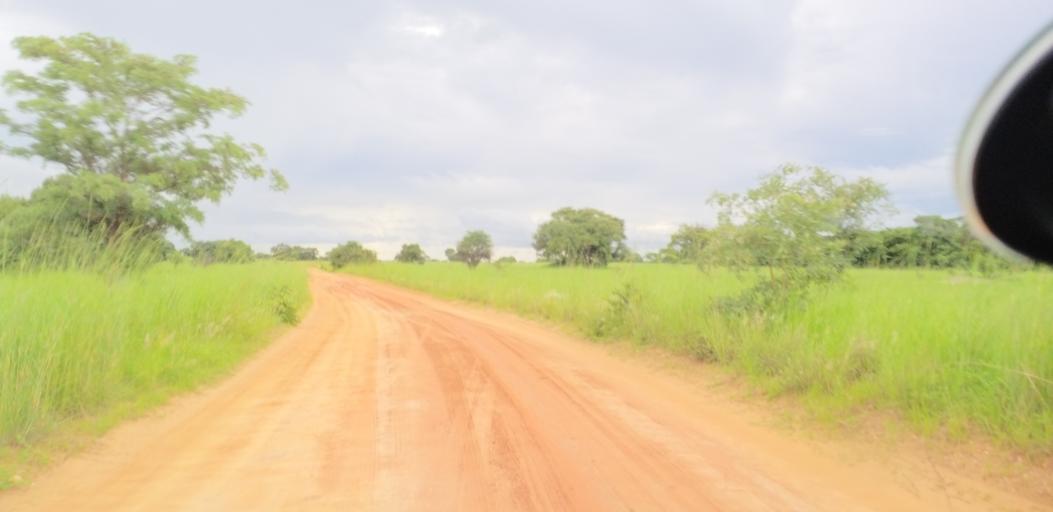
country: ZM
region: Lusaka
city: Chongwe
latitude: -15.1626
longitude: 28.4710
